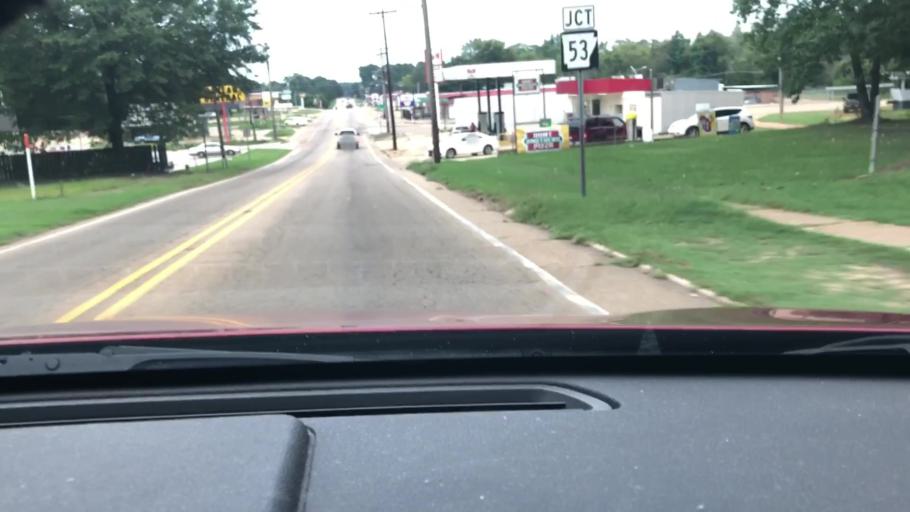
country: US
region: Arkansas
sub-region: Lafayette County
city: Stamps
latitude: 33.3654
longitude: -93.4905
